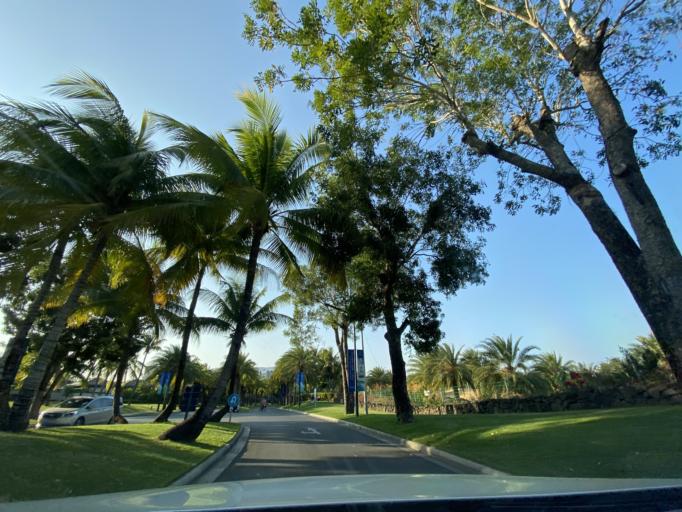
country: CN
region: Hainan
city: Xincun
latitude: 18.4202
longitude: 109.9491
